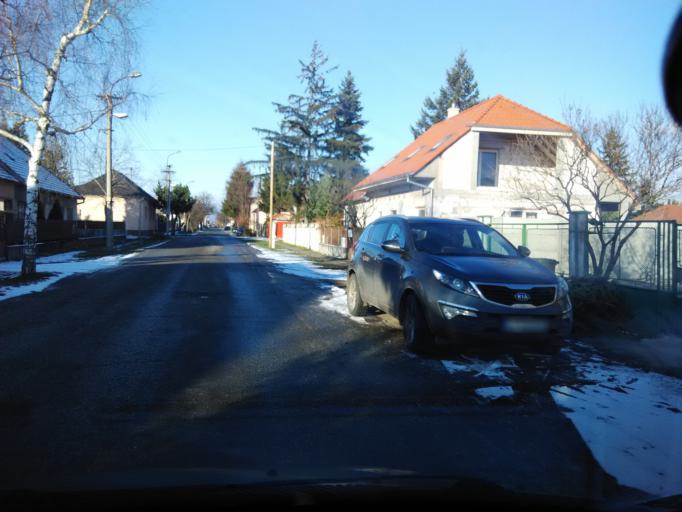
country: SK
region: Nitriansky
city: Levice
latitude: 48.2077
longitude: 18.5870
